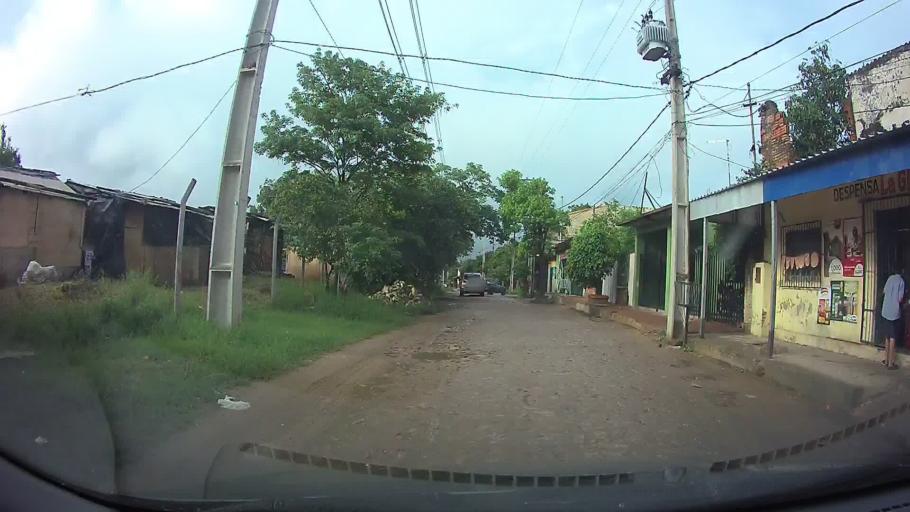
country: PY
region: Asuncion
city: Asuncion
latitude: -25.2469
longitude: -57.5824
